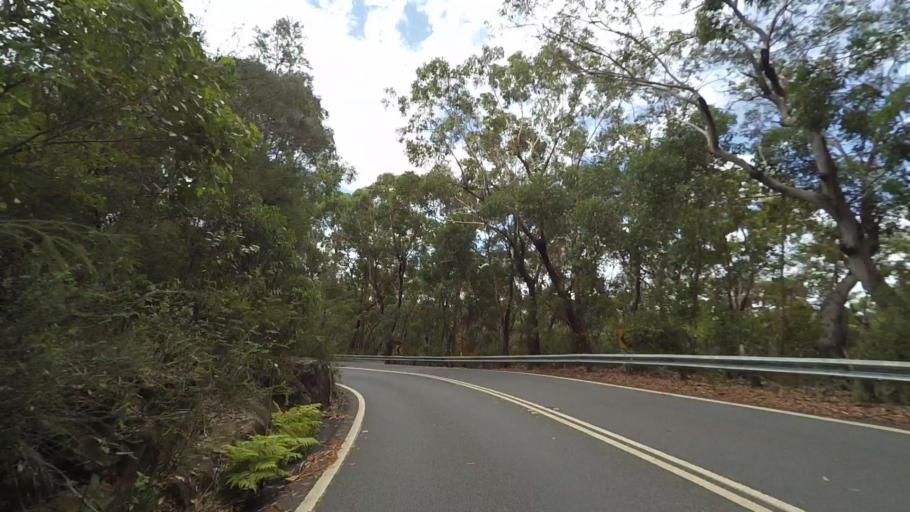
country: AU
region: New South Wales
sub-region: Sutherland Shire
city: Grays Point
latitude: -34.1146
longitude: 151.0650
